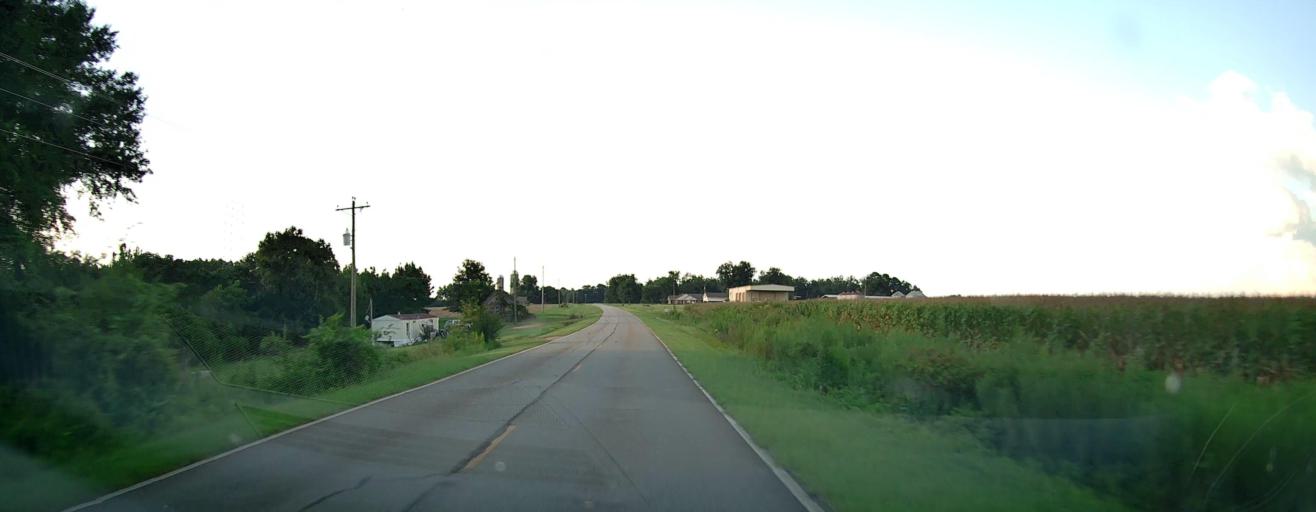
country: US
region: Georgia
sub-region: Peach County
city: Fort Valley
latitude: 32.6055
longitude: -83.8345
